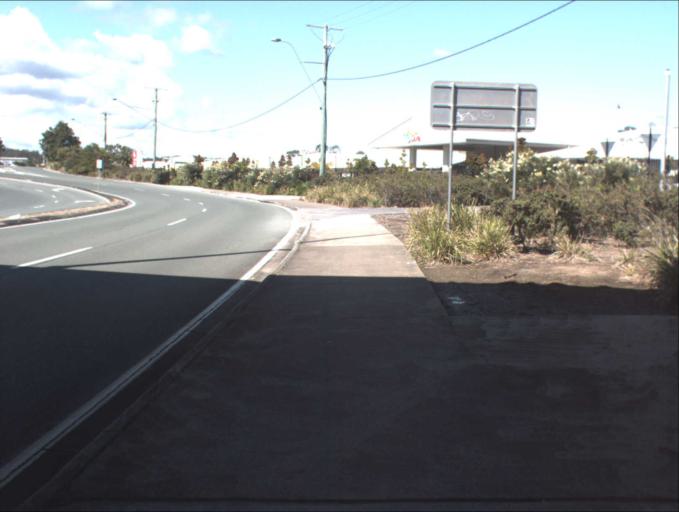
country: AU
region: Queensland
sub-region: Logan
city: Waterford West
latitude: -27.6955
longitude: 153.1538
